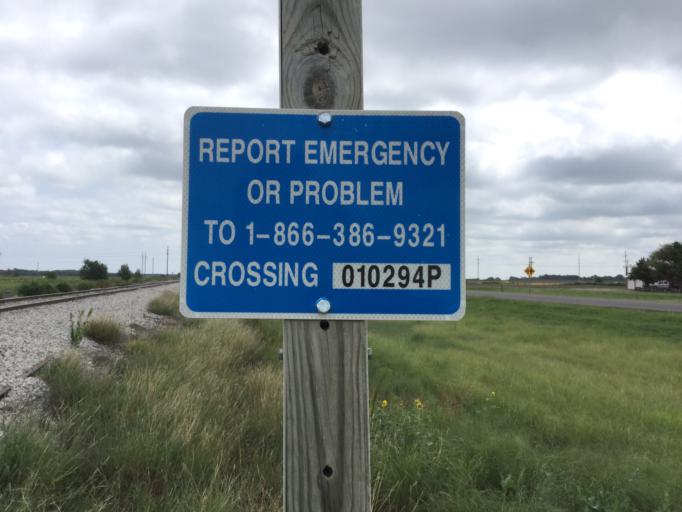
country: US
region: Kansas
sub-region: Rush County
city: La Crosse
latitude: 38.4726
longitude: -99.4411
